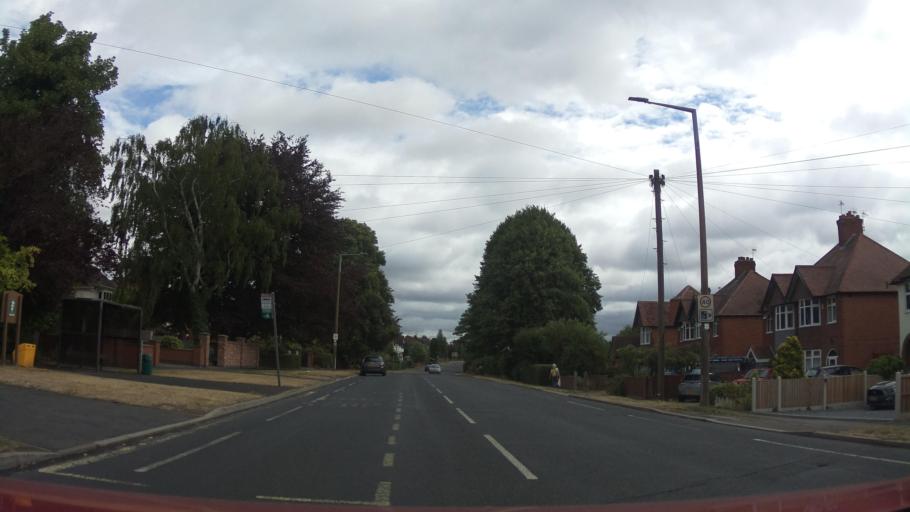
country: GB
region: England
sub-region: Derbyshire
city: Long Eaton
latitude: 52.9179
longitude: -1.3090
